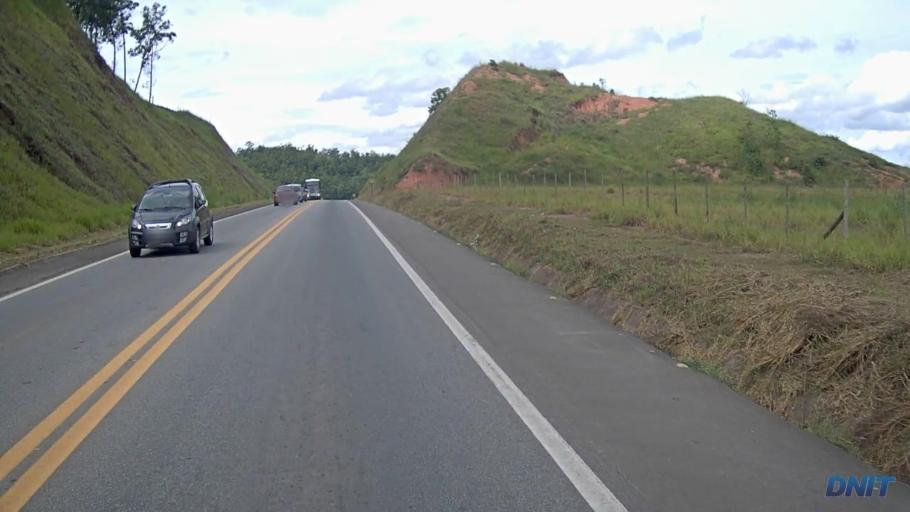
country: BR
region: Minas Gerais
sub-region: Ipatinga
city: Ipatinga
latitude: -19.4509
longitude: -42.5180
